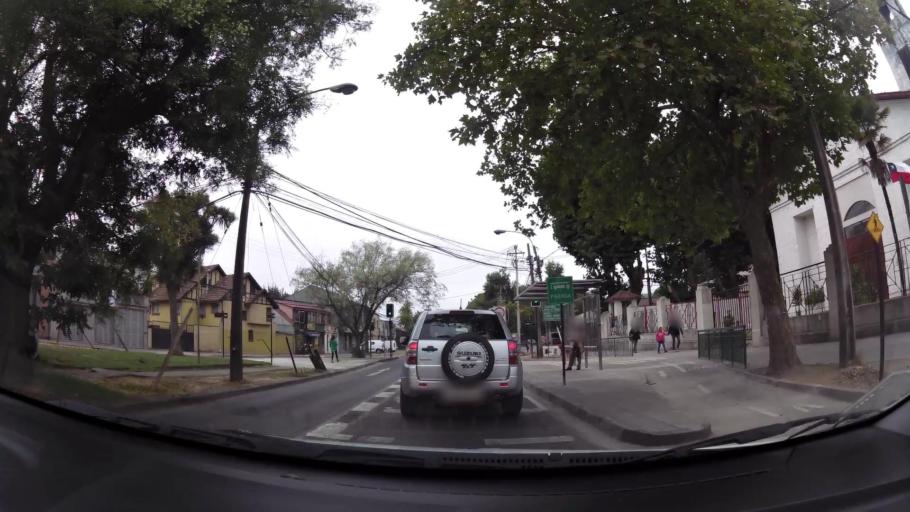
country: CL
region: Biobio
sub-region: Provincia de Concepcion
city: Concepcion
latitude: -36.8170
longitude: -73.0329
